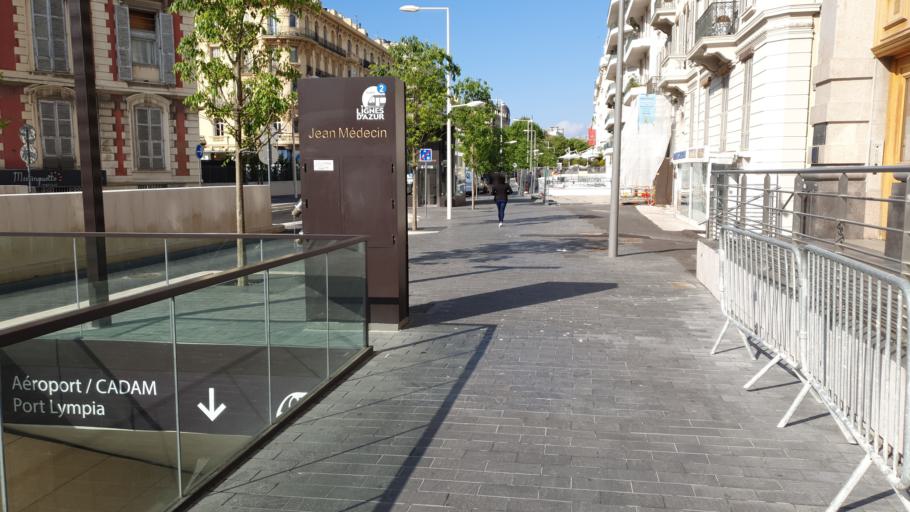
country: FR
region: Provence-Alpes-Cote d'Azur
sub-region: Departement des Alpes-Maritimes
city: Nice
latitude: 43.7005
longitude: 7.2673
